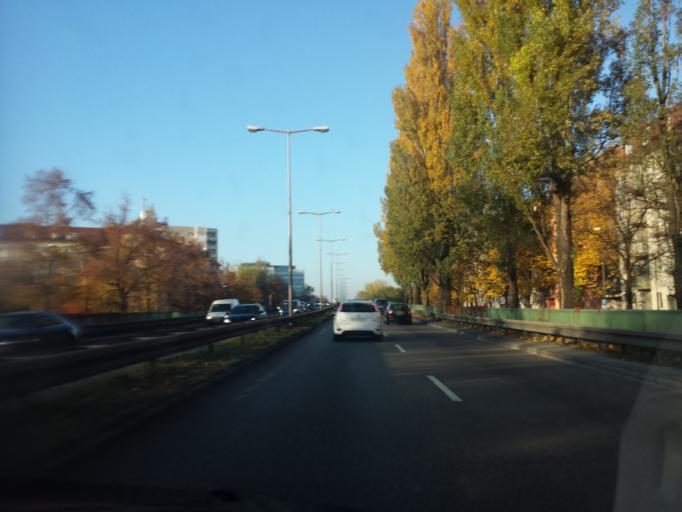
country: DE
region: Bavaria
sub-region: Upper Bavaria
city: Munich
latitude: 48.1636
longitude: 11.5378
